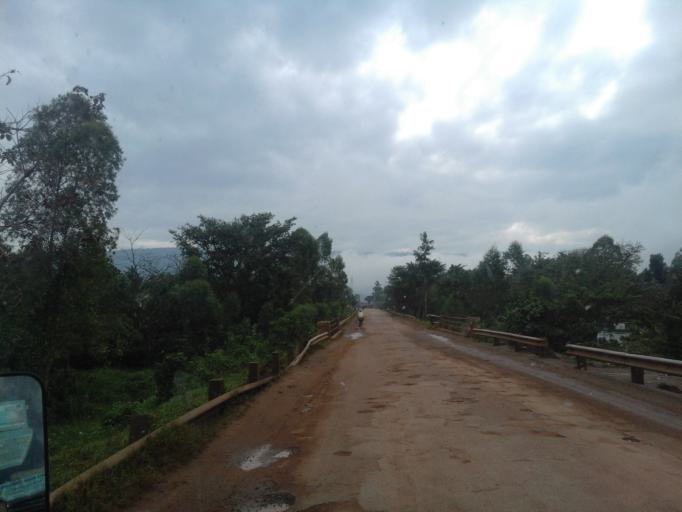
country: UG
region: Eastern Region
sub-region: Sironko District
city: Sironko
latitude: 1.2363
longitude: 34.2567
